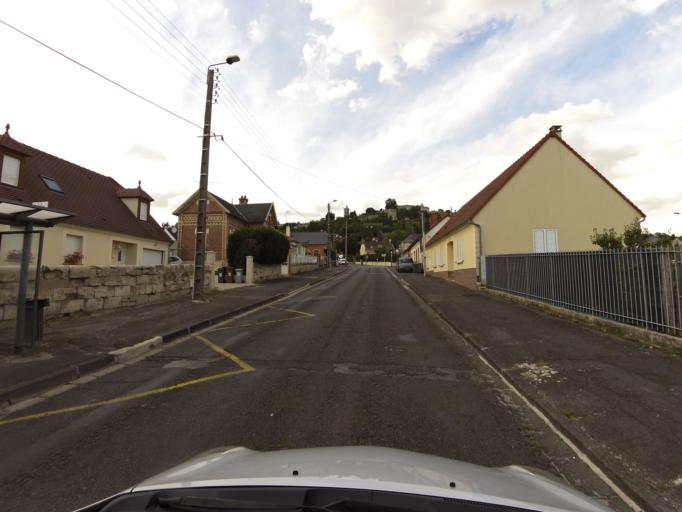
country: FR
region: Picardie
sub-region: Departement de l'Aisne
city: Laon
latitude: 49.5575
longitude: 3.6281
